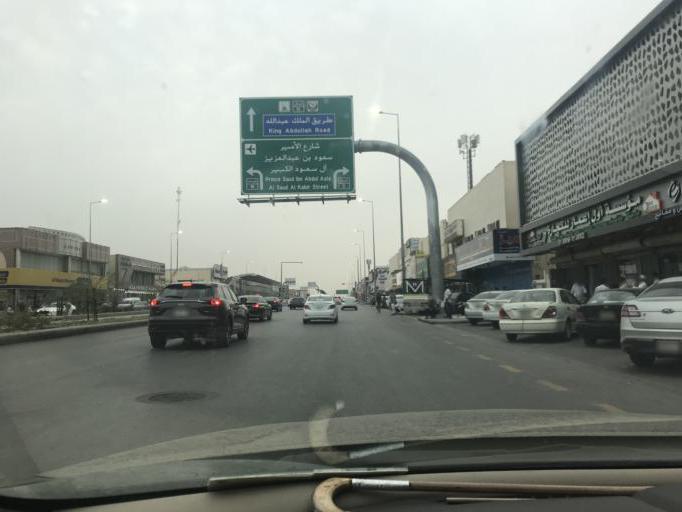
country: SA
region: Ar Riyad
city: Riyadh
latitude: 24.7609
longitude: 46.7644
